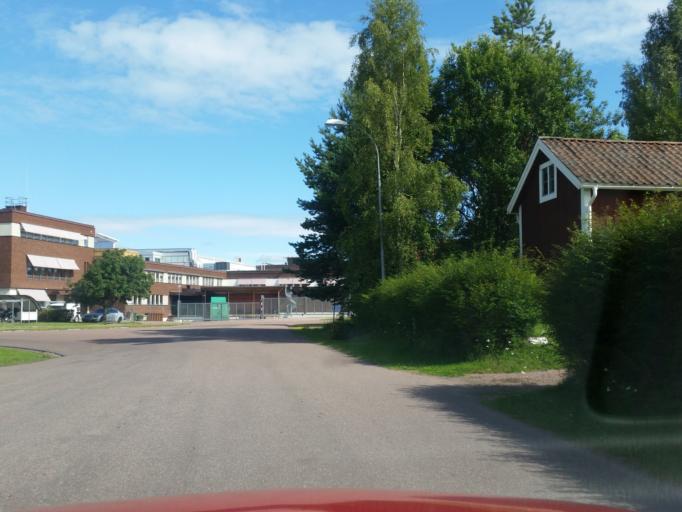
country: SE
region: Dalarna
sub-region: Leksand Municipality
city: Smedby
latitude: 60.6724
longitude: 15.0898
